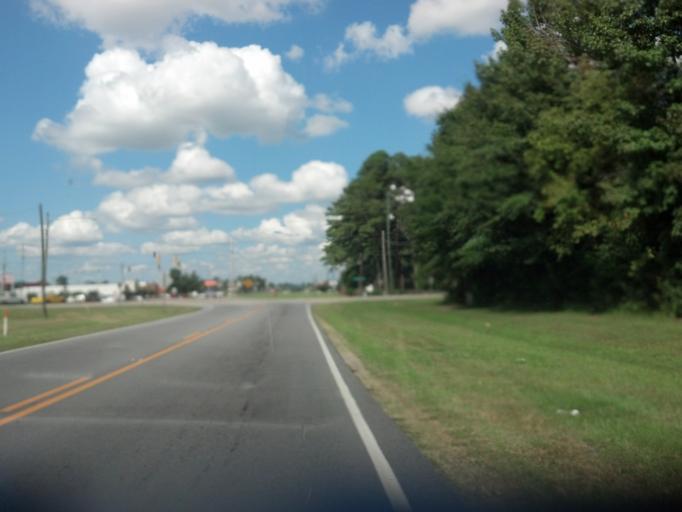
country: US
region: North Carolina
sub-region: Pitt County
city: Winterville
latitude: 35.5413
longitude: -77.4043
